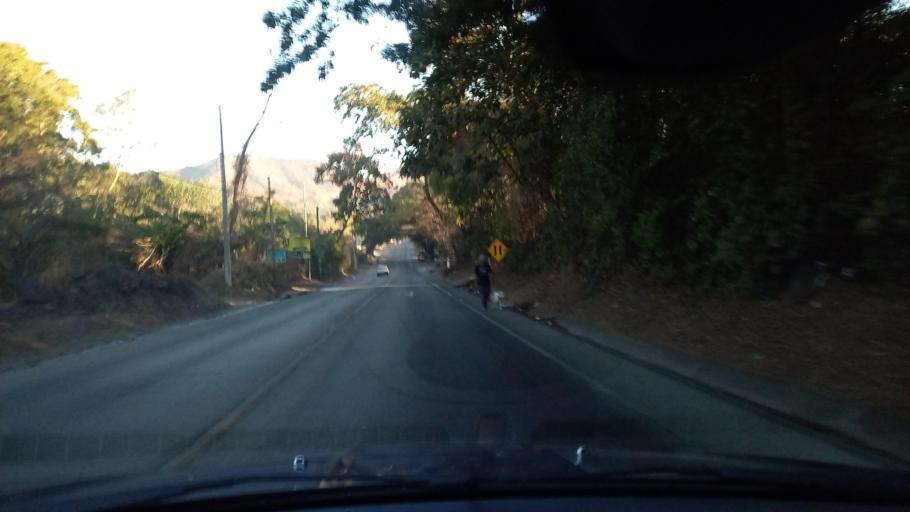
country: SV
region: Santa Ana
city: Santa Ana
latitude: 14.0195
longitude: -89.5364
